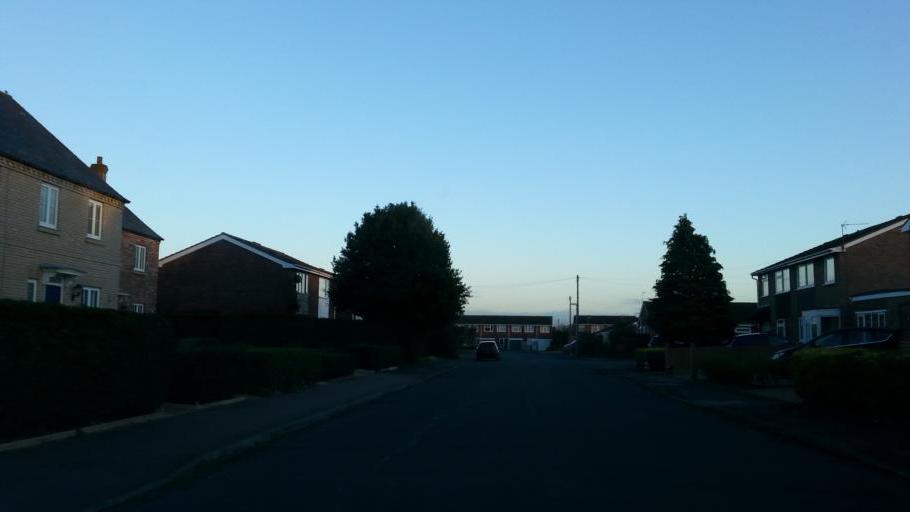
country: GB
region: England
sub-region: Cambridgeshire
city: Hemingford Grey
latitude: 52.3001
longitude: -0.0652
